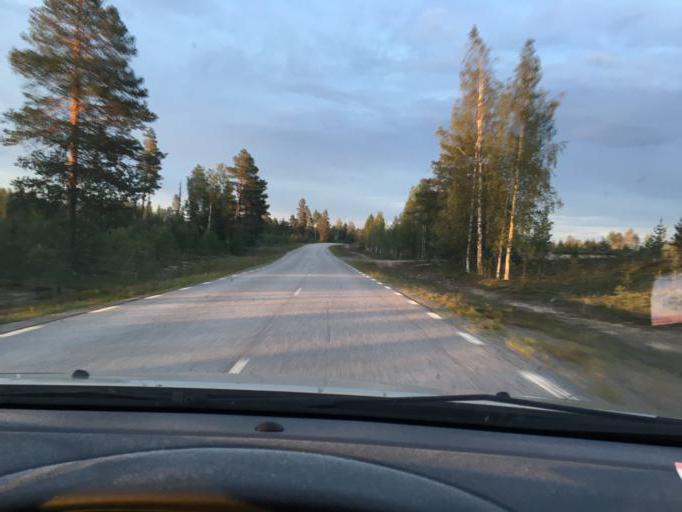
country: SE
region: Norrbotten
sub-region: Kalix Kommun
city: Toere
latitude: 66.0529
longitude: 22.4775
